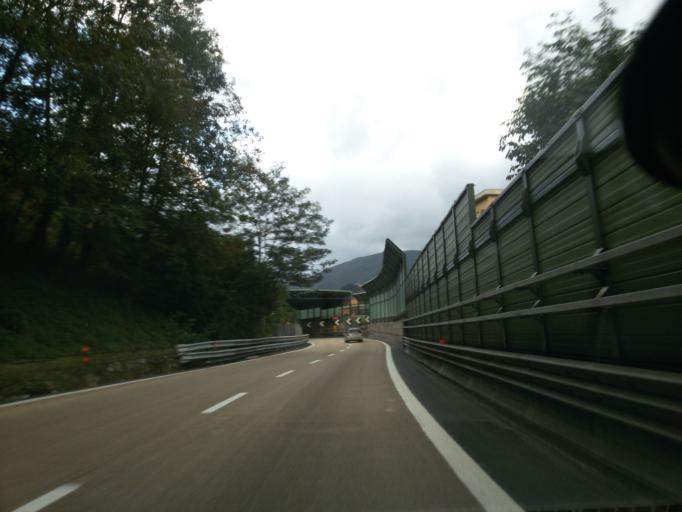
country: IT
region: Liguria
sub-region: Provincia di Genova
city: Manesseno
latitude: 44.4638
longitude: 8.9045
